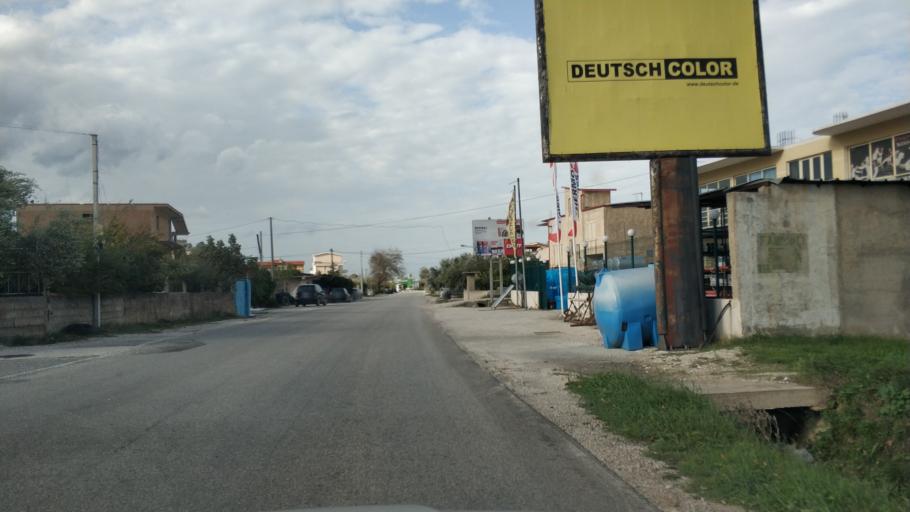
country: AL
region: Vlore
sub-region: Rrethi i Vlores
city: Orikum
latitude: 40.3265
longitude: 19.4788
